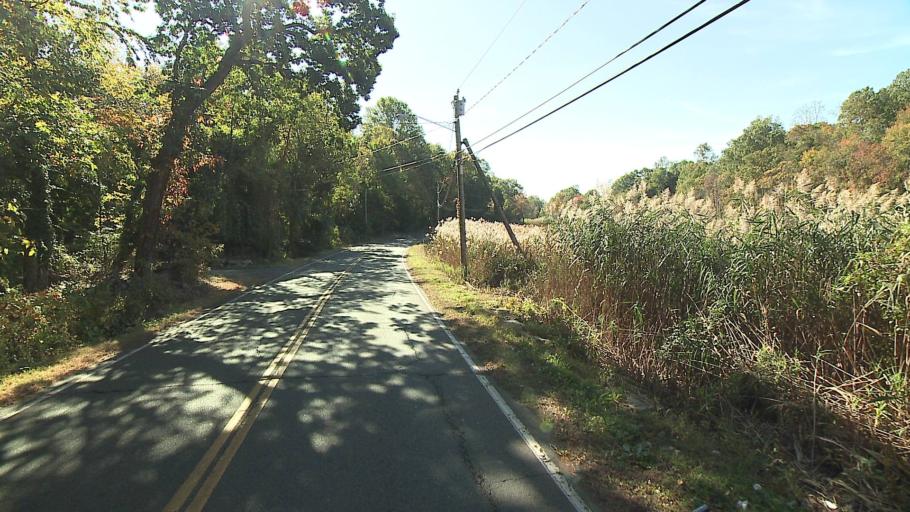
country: US
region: Connecticut
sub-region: Fairfield County
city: Darien
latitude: 41.0742
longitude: -73.4276
